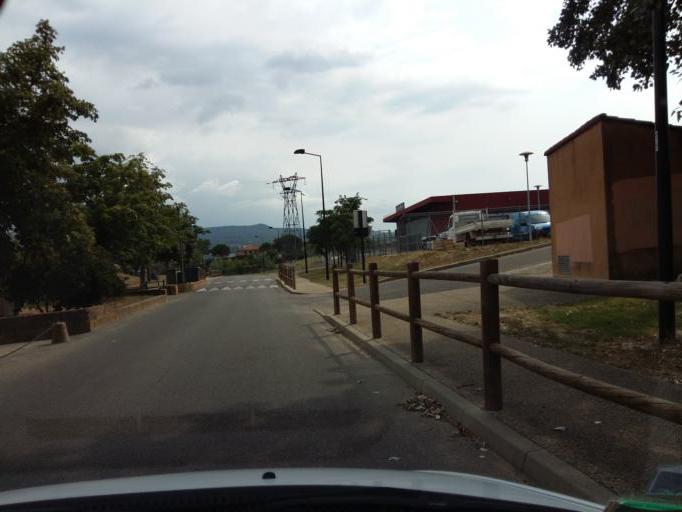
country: FR
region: Provence-Alpes-Cote d'Azur
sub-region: Departement du Vaucluse
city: Gargas
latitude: 43.8914
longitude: 5.3770
